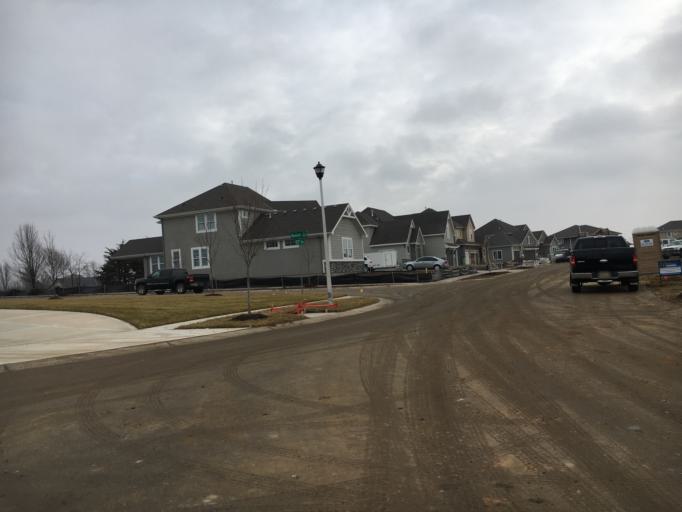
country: US
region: Kansas
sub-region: Johnson County
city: Olathe
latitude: 38.8067
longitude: -94.6921
